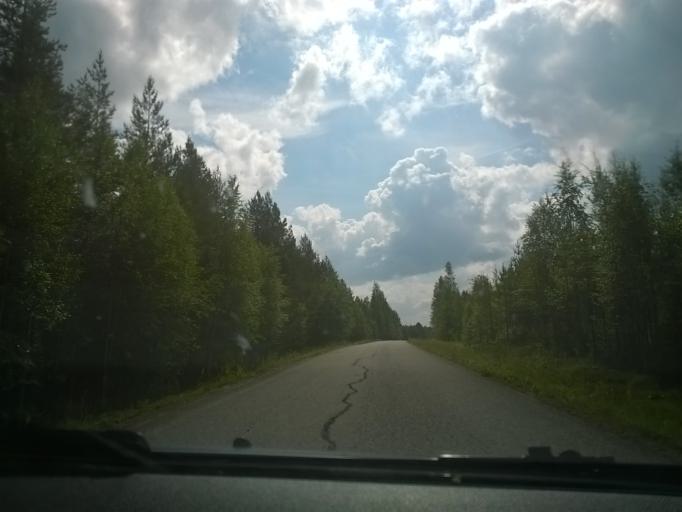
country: FI
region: Kainuu
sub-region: Kehys-Kainuu
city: Kuhmo
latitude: 64.4165
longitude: 29.7648
